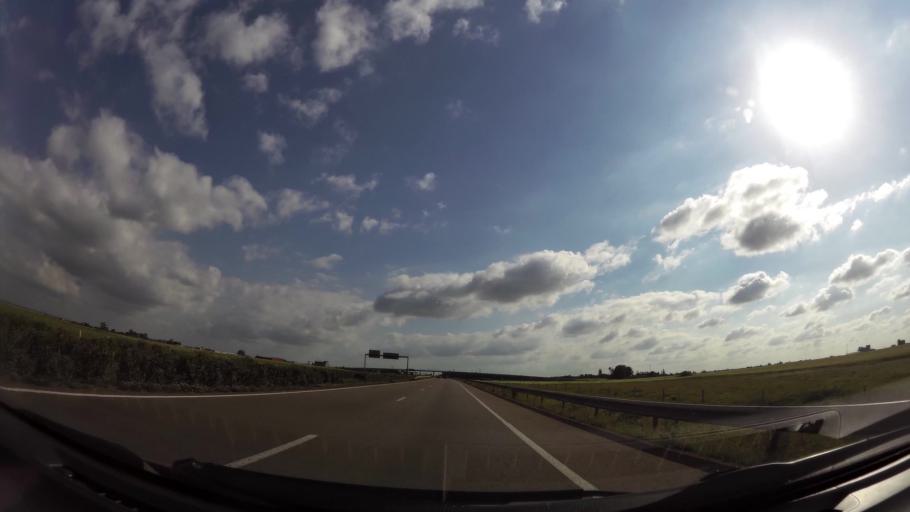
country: MA
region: Chaouia-Ouardigha
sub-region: Settat Province
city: Berrechid
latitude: 33.2414
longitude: -7.5681
